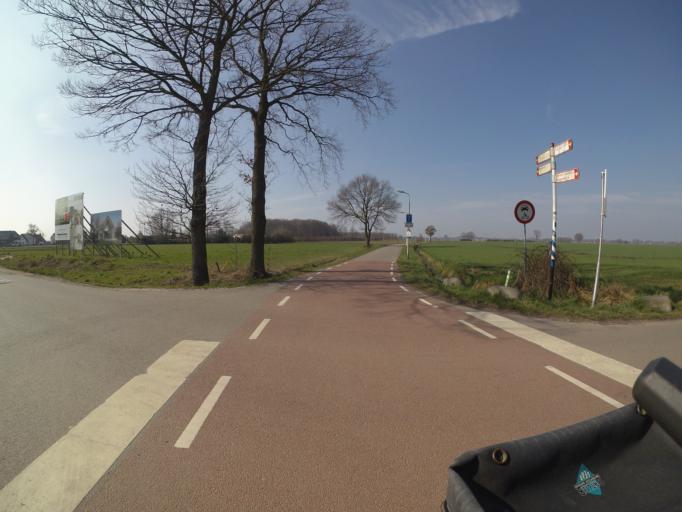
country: NL
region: North Brabant
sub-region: Gemeente Tilburg
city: Tilburg
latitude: 51.5926
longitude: 5.1299
